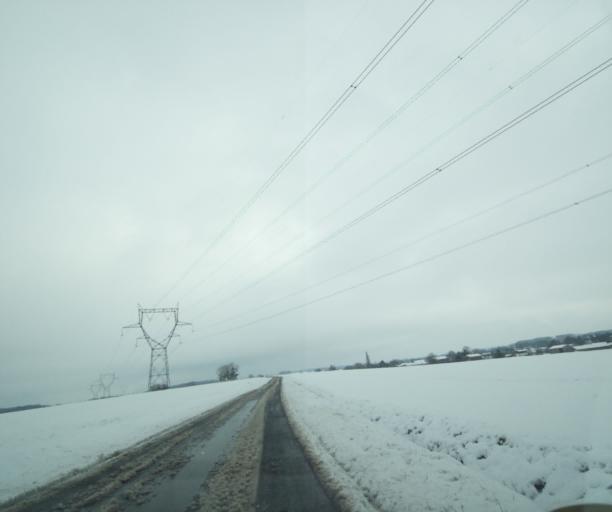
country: FR
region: Champagne-Ardenne
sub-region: Departement de la Haute-Marne
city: Montier-en-Der
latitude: 48.5085
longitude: 4.7172
